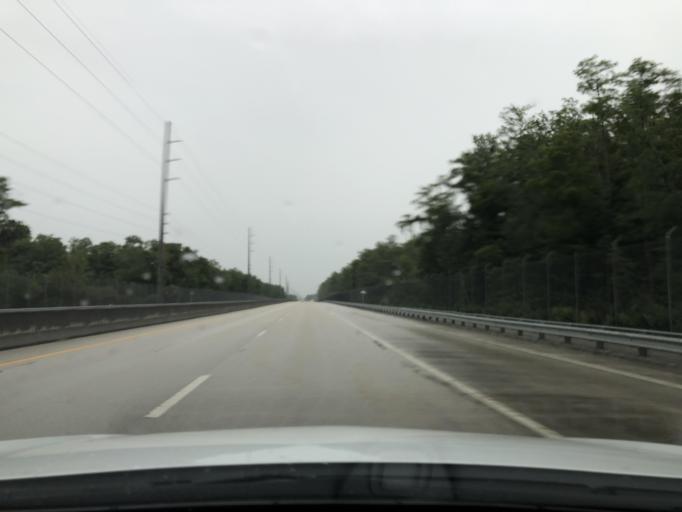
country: US
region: Florida
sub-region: Collier County
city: Orangetree
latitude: 26.2940
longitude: -81.4726
